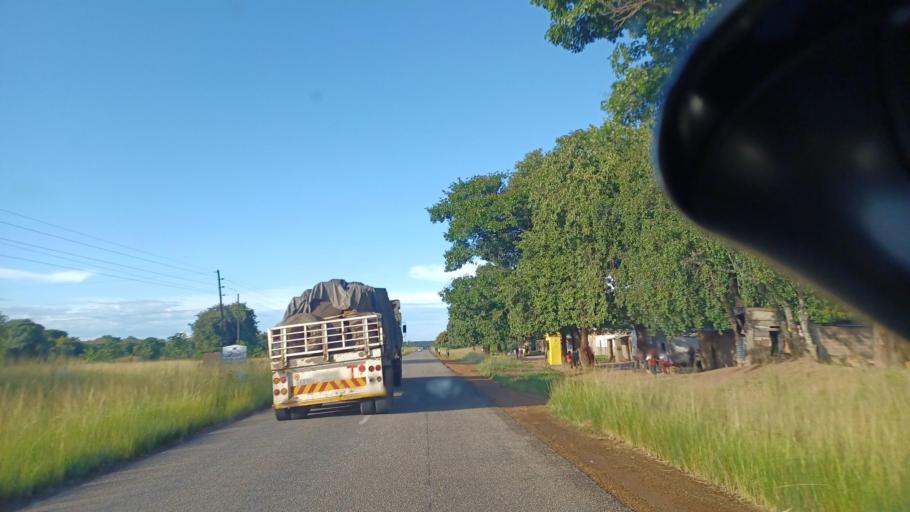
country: ZM
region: North-Western
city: Kalengwa
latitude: -13.2175
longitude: 24.7593
